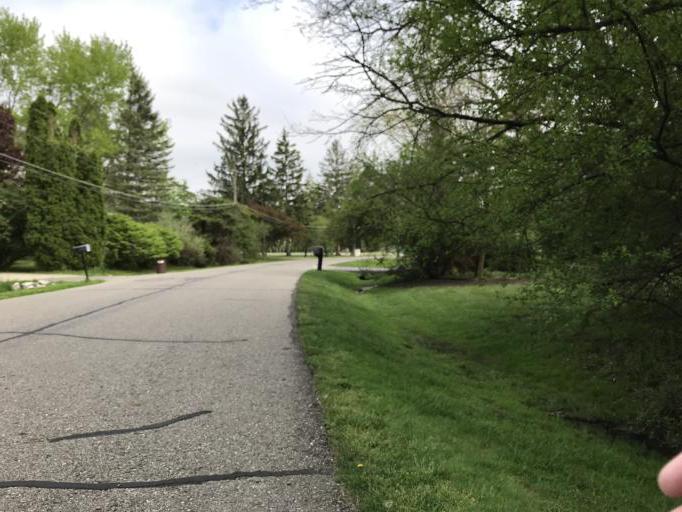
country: US
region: Michigan
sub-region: Oakland County
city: Farmington
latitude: 42.4719
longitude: -83.3243
